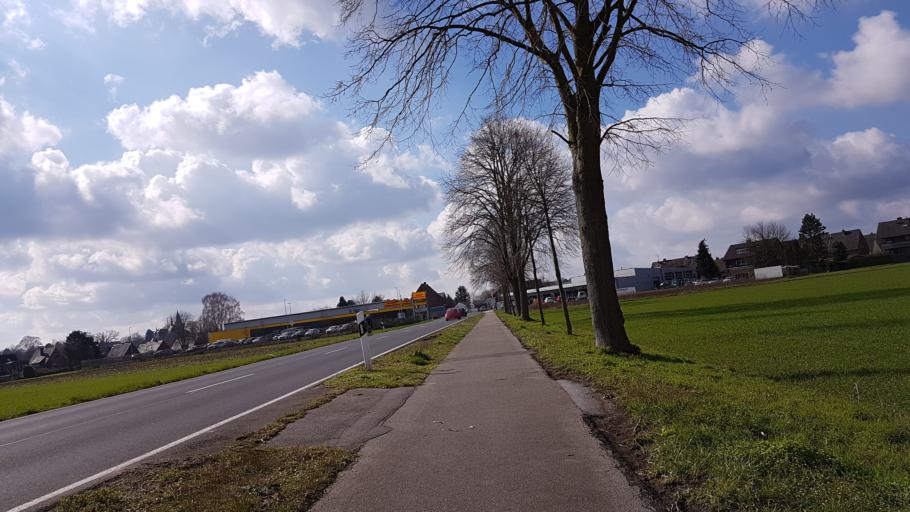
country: DE
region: North Rhine-Westphalia
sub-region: Regierungsbezirk Dusseldorf
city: Niederkruchten
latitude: 51.2042
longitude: 6.2221
